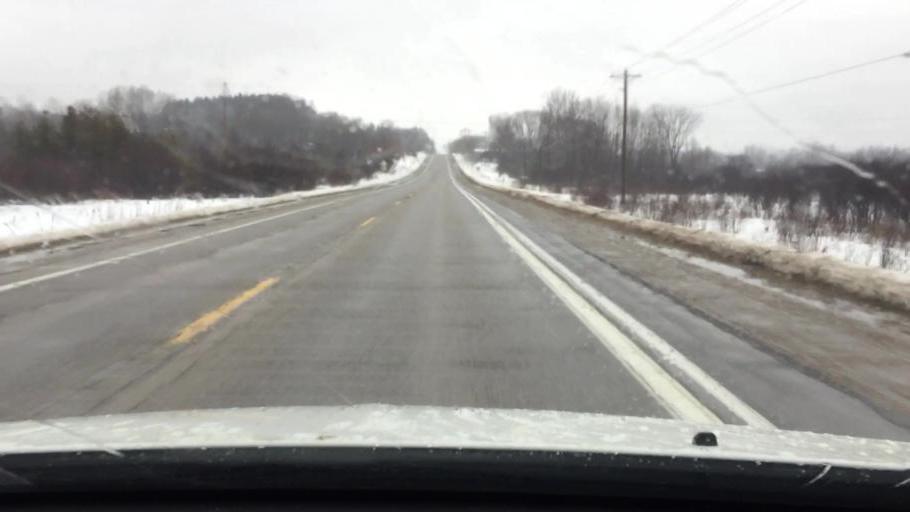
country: US
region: Michigan
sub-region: Charlevoix County
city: East Jordan
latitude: 45.1350
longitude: -85.1397
